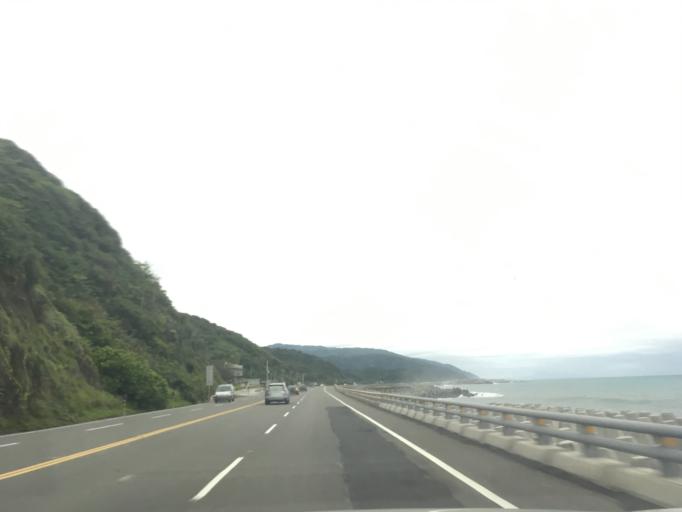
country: TW
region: Taiwan
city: Hengchun
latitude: 22.3210
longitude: 120.8918
